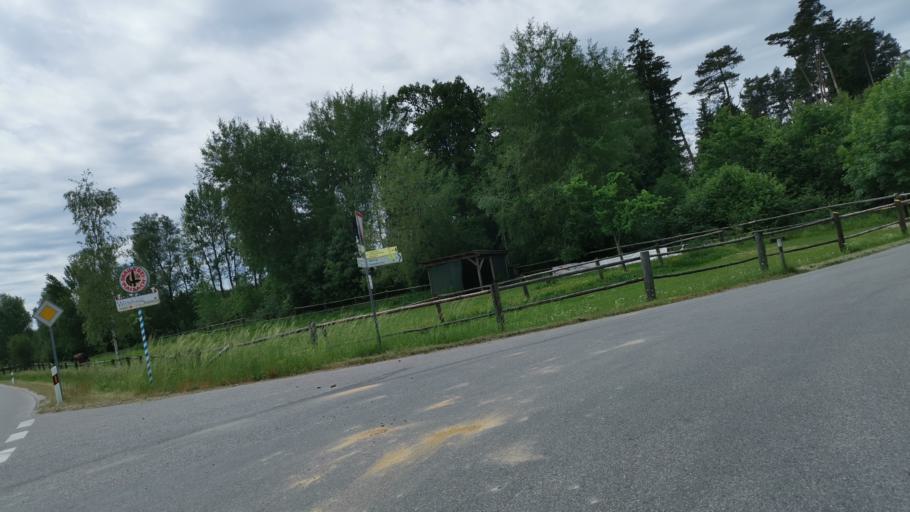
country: DE
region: Bavaria
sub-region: Upper Bavaria
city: Hattenhofen
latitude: 48.2200
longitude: 11.0991
